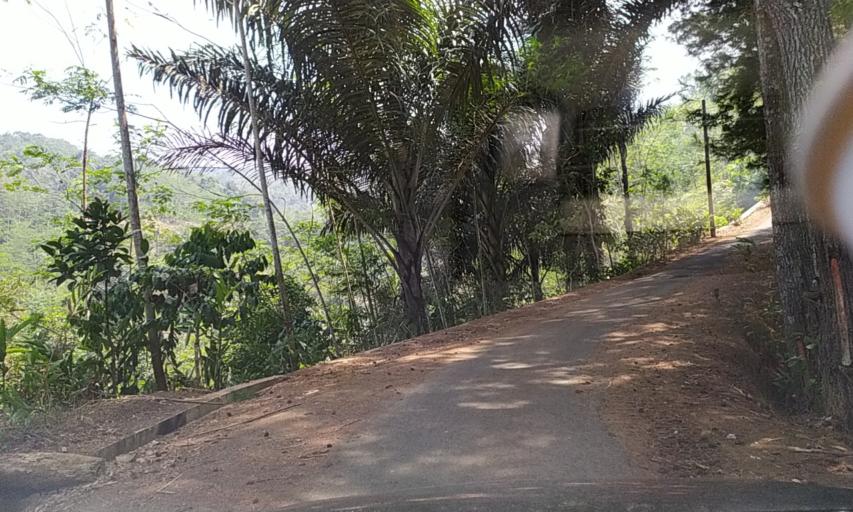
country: ID
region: Central Java
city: Cilumping
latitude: -7.1880
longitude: 108.6165
